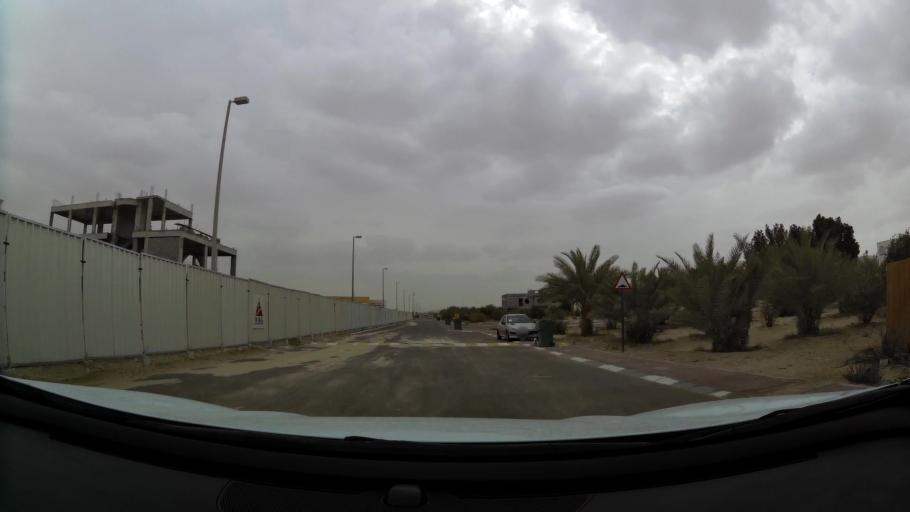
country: AE
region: Abu Dhabi
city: Abu Dhabi
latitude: 24.3317
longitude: 54.6455
